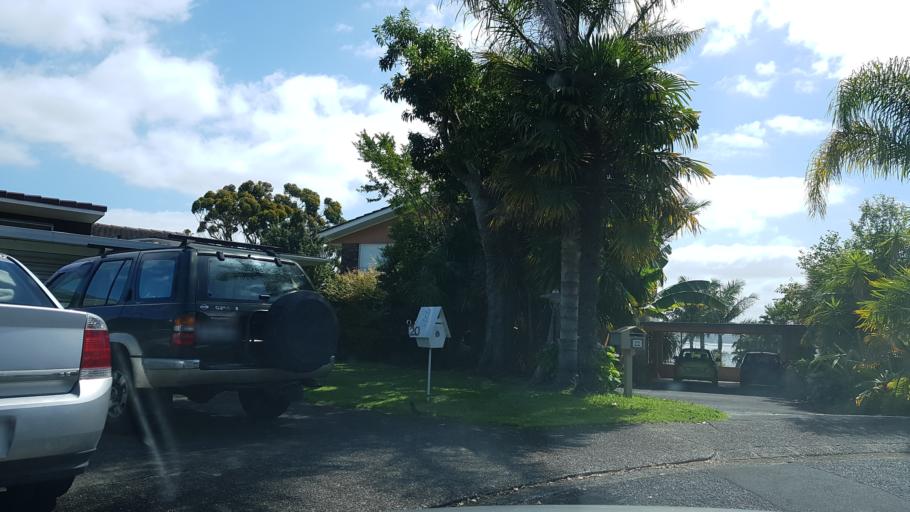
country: NZ
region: Auckland
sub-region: Auckland
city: North Shore
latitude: -36.8122
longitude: 174.6912
